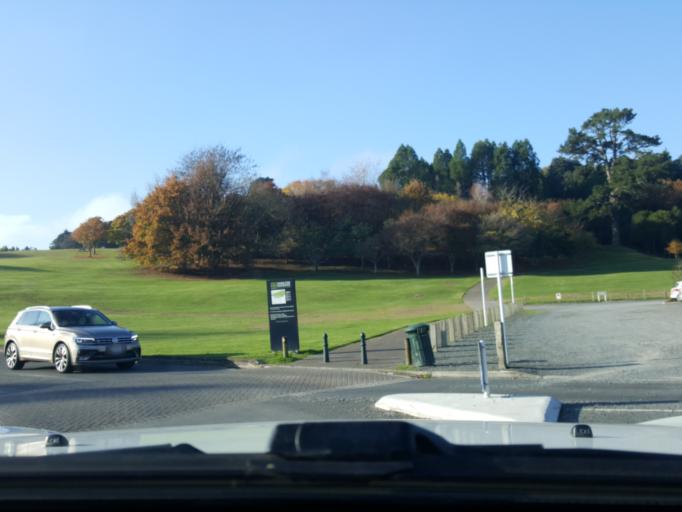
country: NZ
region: Waikato
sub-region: Hamilton City
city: Hamilton
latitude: -37.8059
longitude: 175.3048
